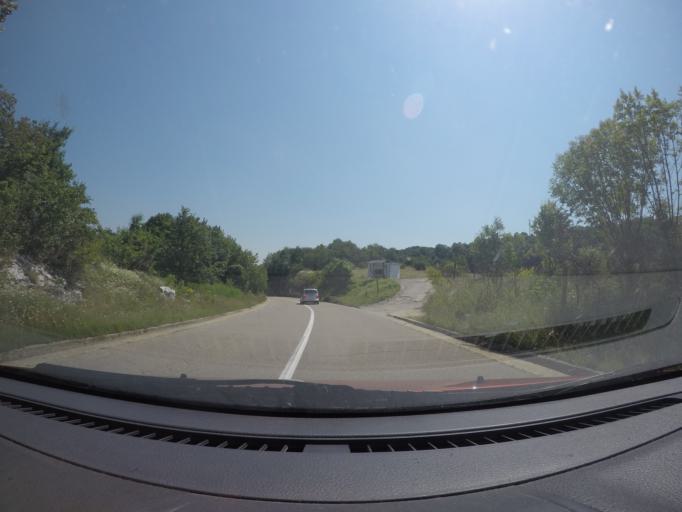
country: RO
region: Mehedinti
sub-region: Comuna Eselnita
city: Eselnita
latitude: 44.6619
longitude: 22.3295
